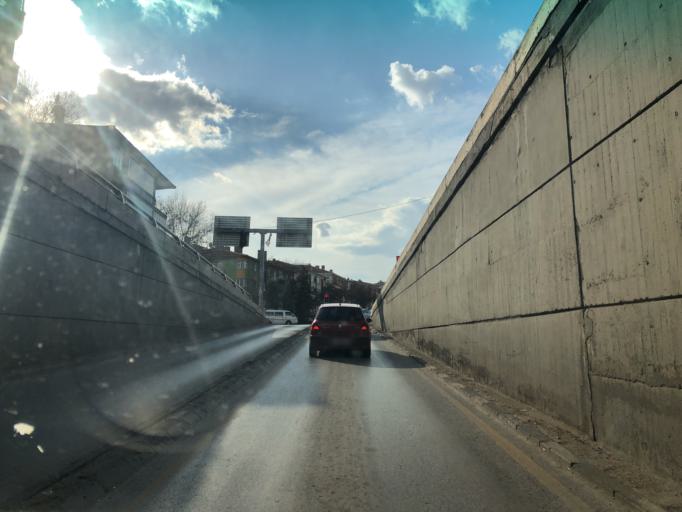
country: TR
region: Ankara
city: Ankara
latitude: 39.9845
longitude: 32.8581
